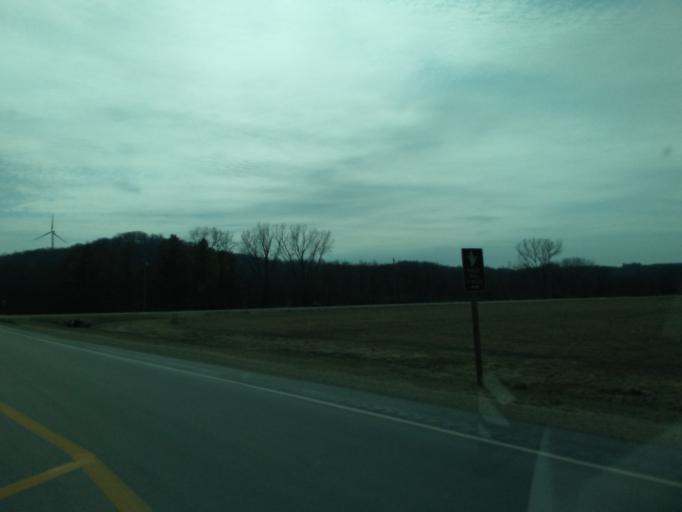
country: US
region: Iowa
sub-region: Winneshiek County
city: Decorah
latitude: 43.3218
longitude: -91.8137
